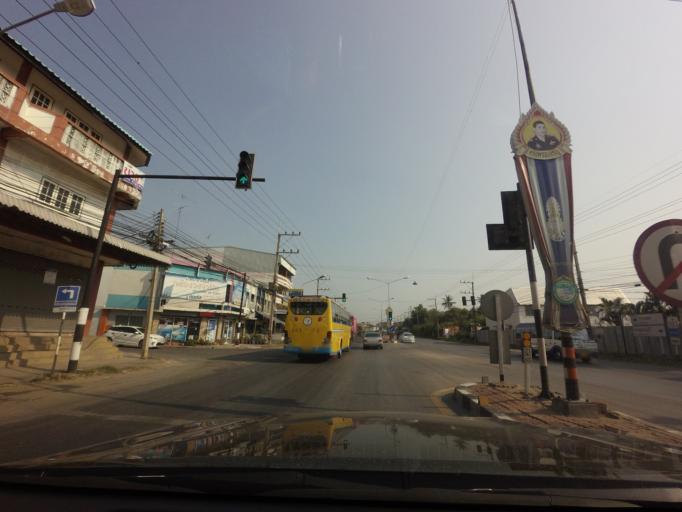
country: TH
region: Kanchanaburi
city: Tha Maka
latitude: 13.8859
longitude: 99.8013
